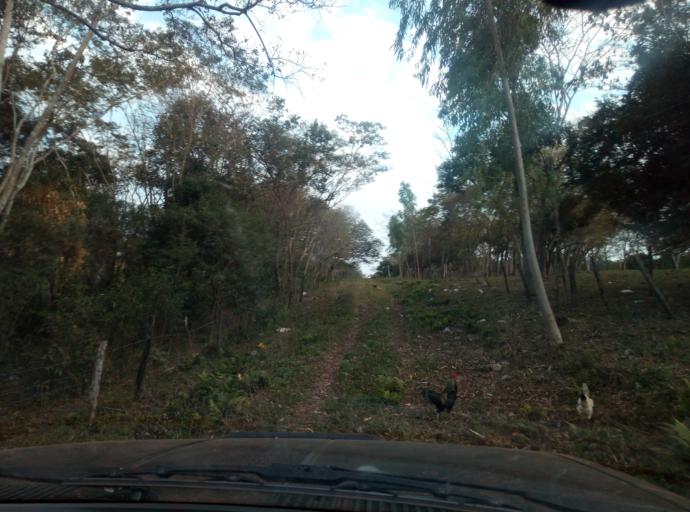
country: PY
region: Caaguazu
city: Doctor Cecilio Baez
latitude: -25.1871
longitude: -56.1298
